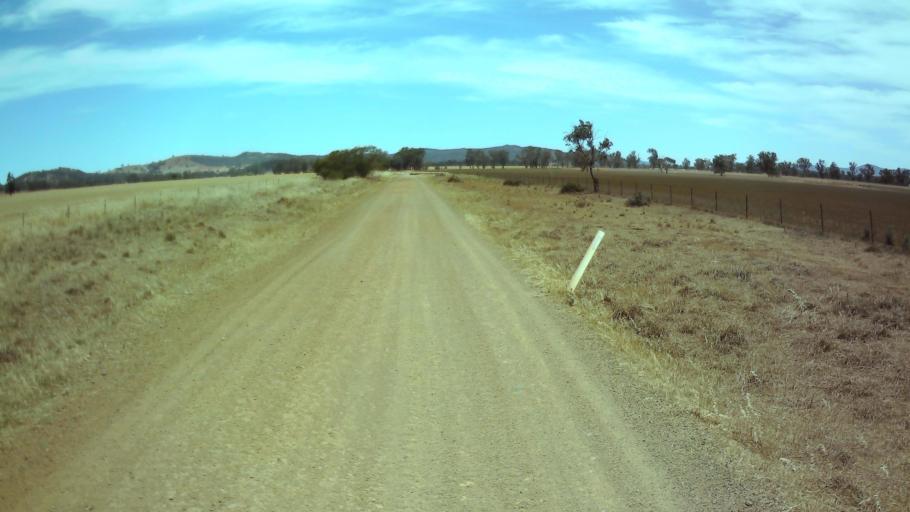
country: AU
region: New South Wales
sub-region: Weddin
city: Grenfell
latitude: -33.7493
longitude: 148.1446
